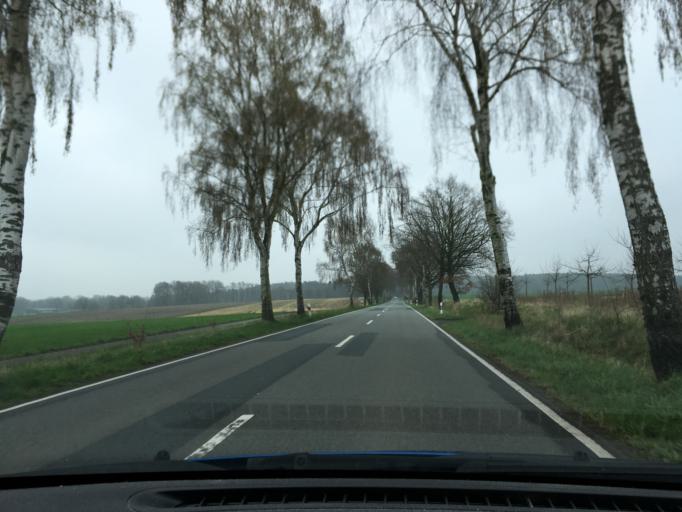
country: DE
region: Lower Saxony
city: Neetze
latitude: 53.2667
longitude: 10.6419
